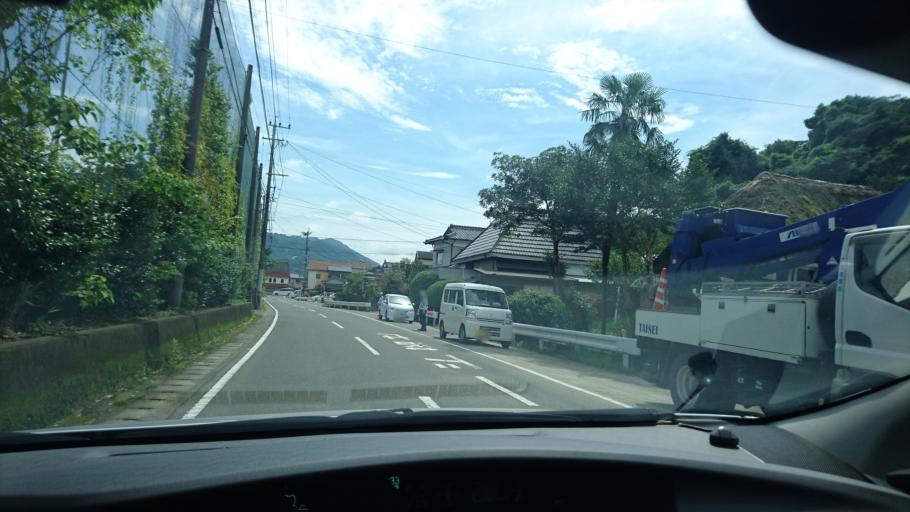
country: JP
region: Saga Prefecture
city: Takeocho-takeo
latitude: 33.2218
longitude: 130.0722
